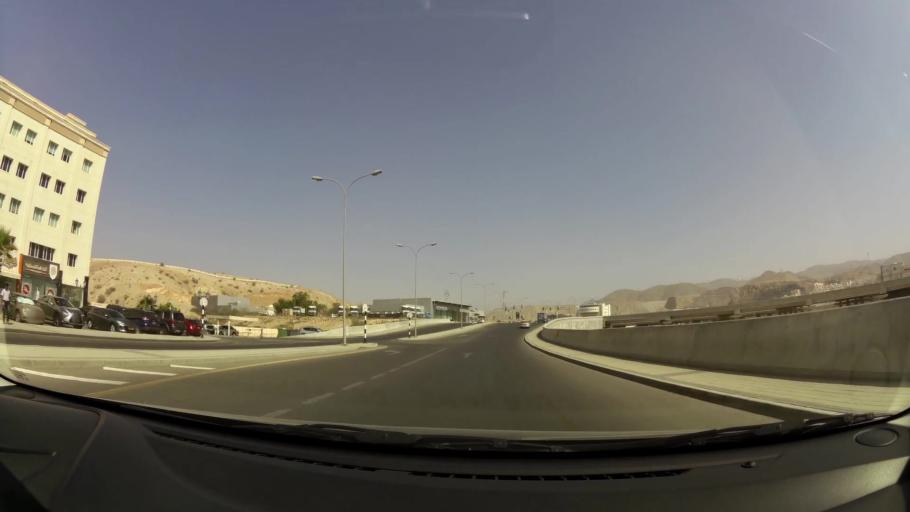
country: OM
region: Muhafazat Masqat
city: Muscat
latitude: 23.6122
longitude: 58.4984
